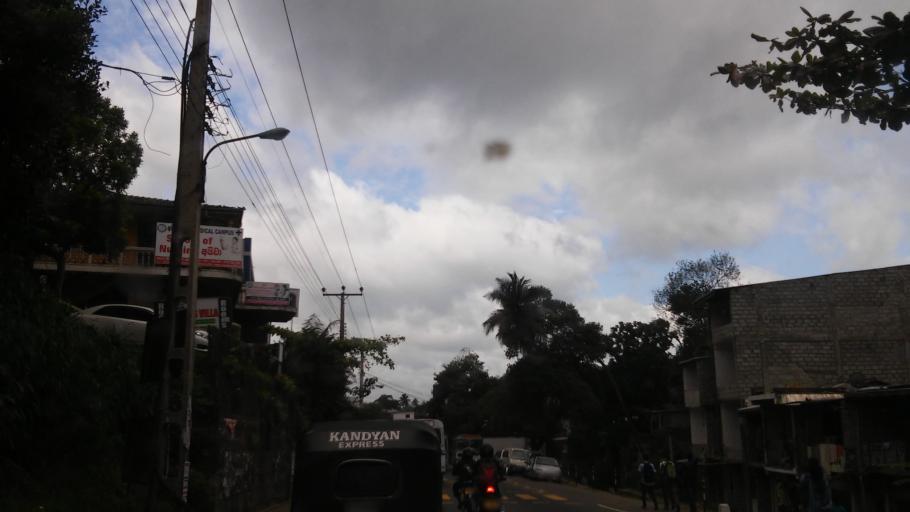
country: LK
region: Central
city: Kandy
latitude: 7.2864
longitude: 80.6292
